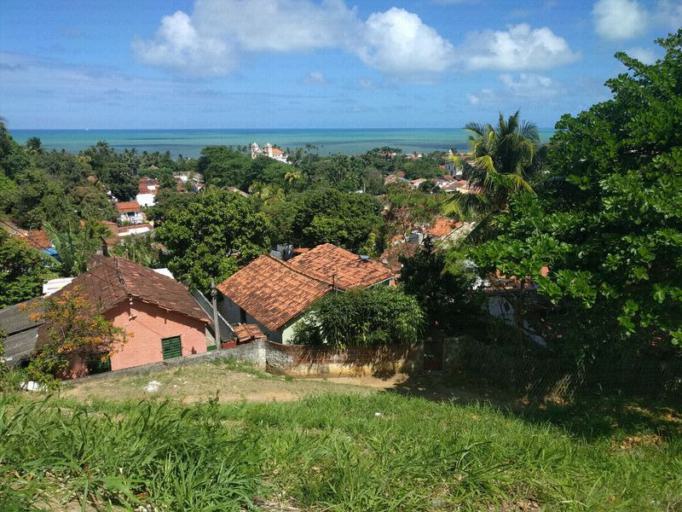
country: BR
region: Pernambuco
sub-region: Olinda
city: Olinda
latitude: -8.0132
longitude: -34.8521
